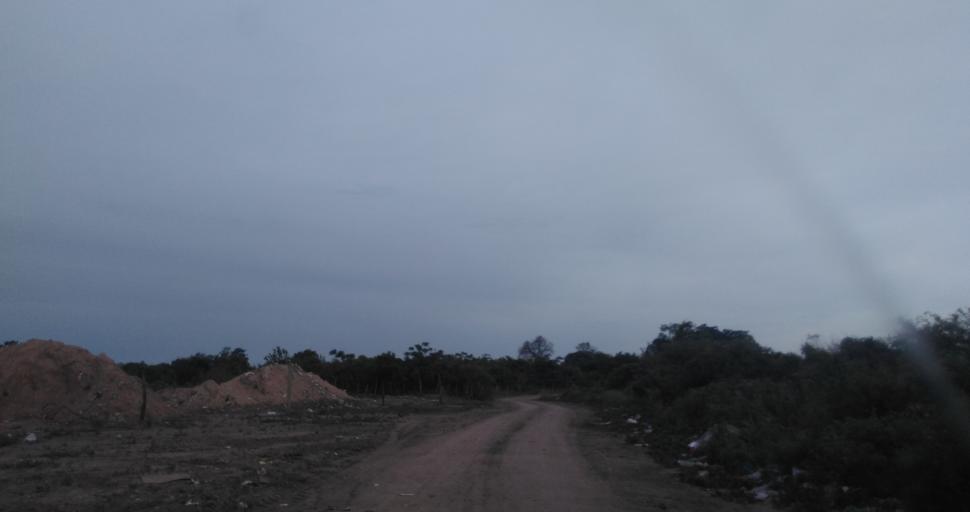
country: AR
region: Chaco
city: Fontana
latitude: -27.4042
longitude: -59.0211
